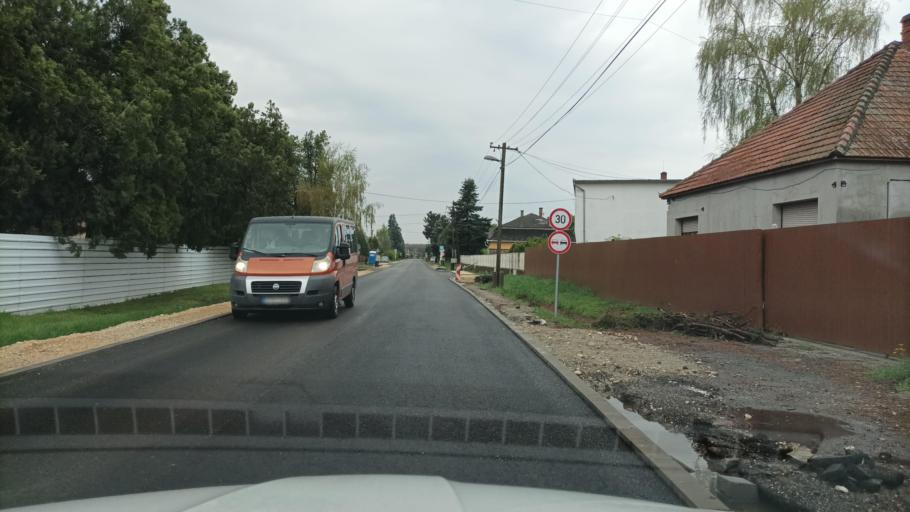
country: HU
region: Pest
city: Danszentmiklos
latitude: 47.2074
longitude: 19.5653
